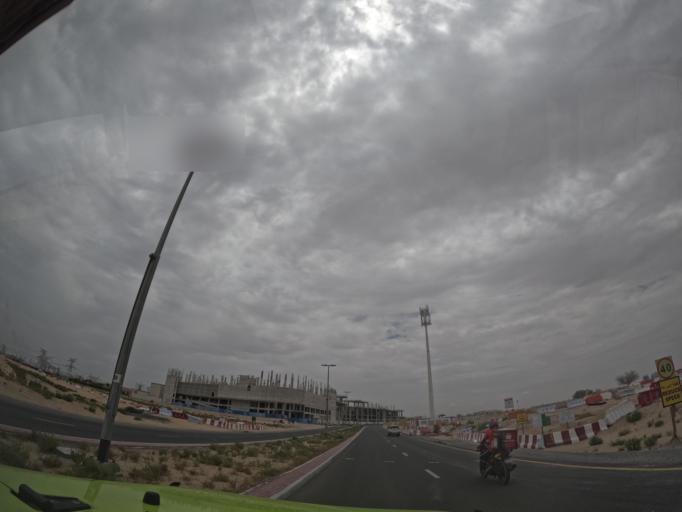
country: AE
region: Ash Shariqah
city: Sharjah
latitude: 25.1600
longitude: 55.3669
